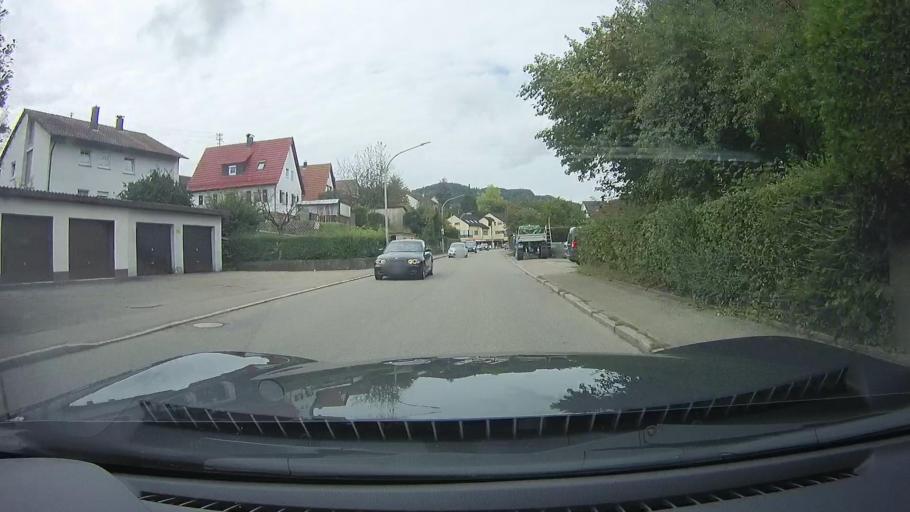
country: DE
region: Baden-Wuerttemberg
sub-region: Regierungsbezirk Stuttgart
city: Murrhardt
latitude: 48.9813
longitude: 9.5684
